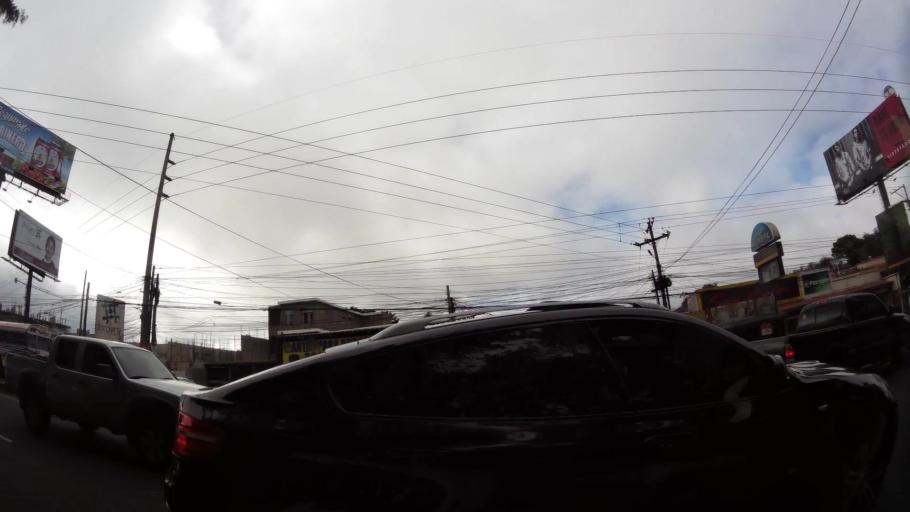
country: GT
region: Guatemala
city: Santa Catarina Pinula
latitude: 14.5587
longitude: -90.4598
